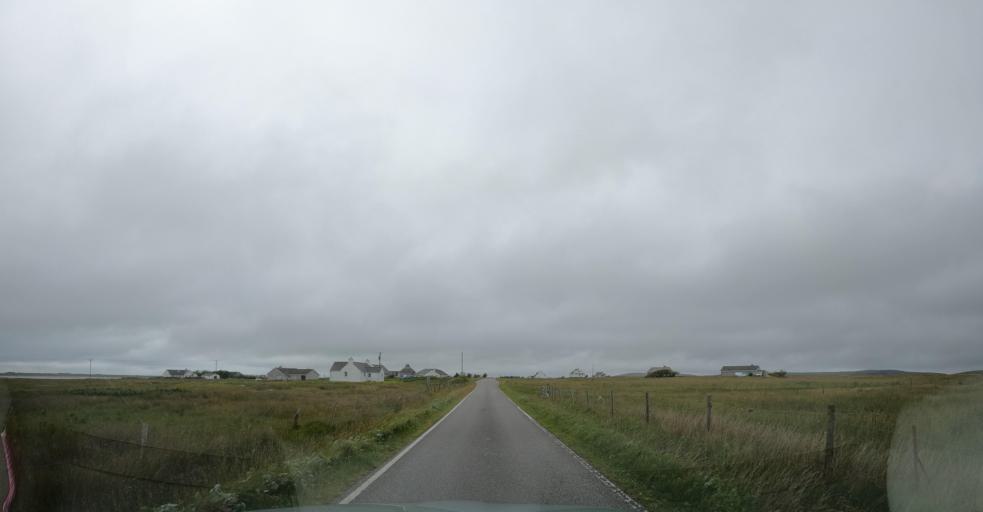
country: GB
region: Scotland
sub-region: Eilean Siar
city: Isle of North Uist
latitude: 57.5688
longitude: -7.3917
